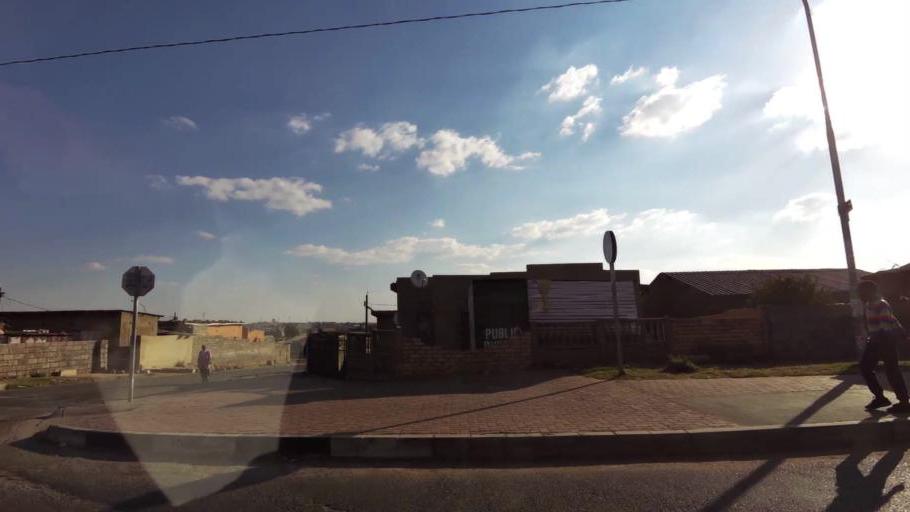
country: ZA
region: Gauteng
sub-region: City of Johannesburg Metropolitan Municipality
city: Roodepoort
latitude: -26.2163
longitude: 27.8854
